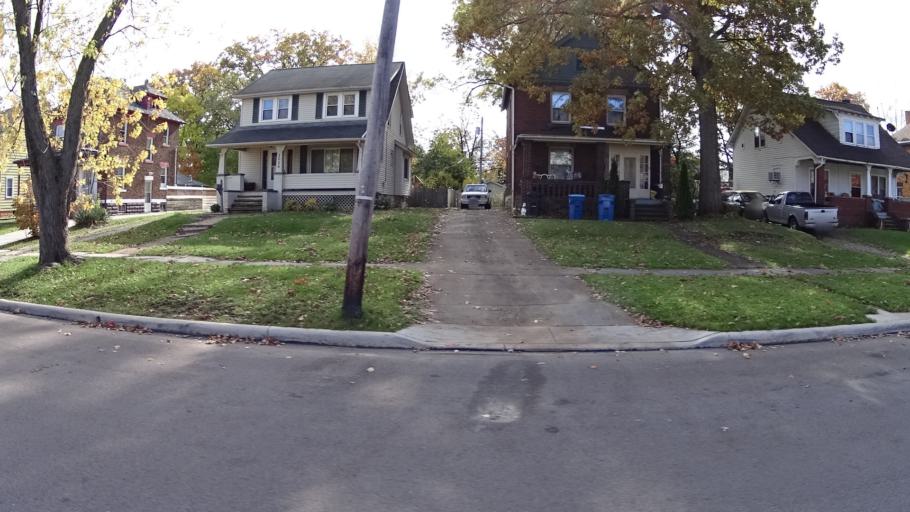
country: US
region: Ohio
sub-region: Lorain County
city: Sheffield
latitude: 41.4436
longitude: -82.1264
